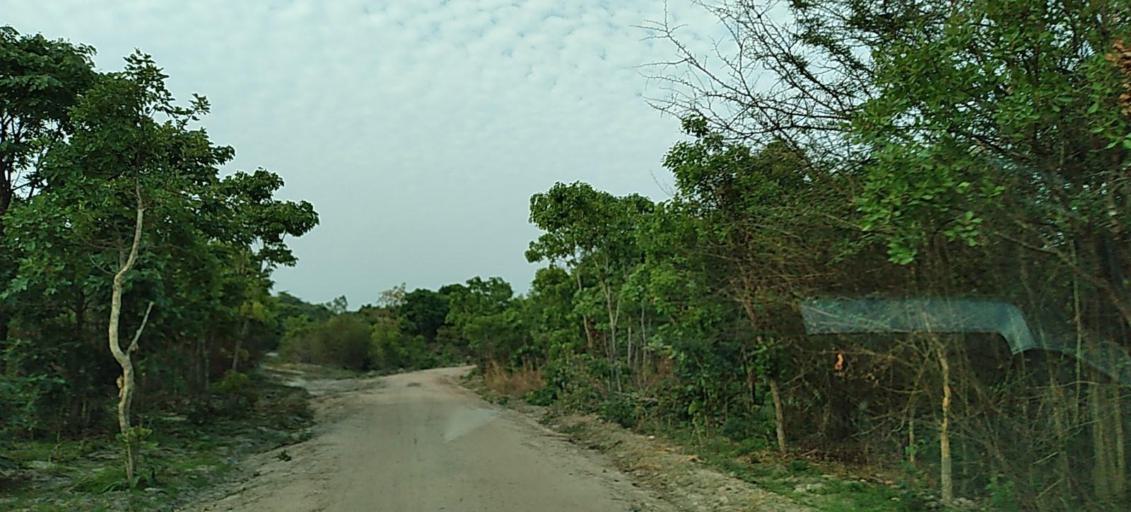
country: ZM
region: Copperbelt
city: Kalulushi
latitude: -12.8955
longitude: 27.6873
